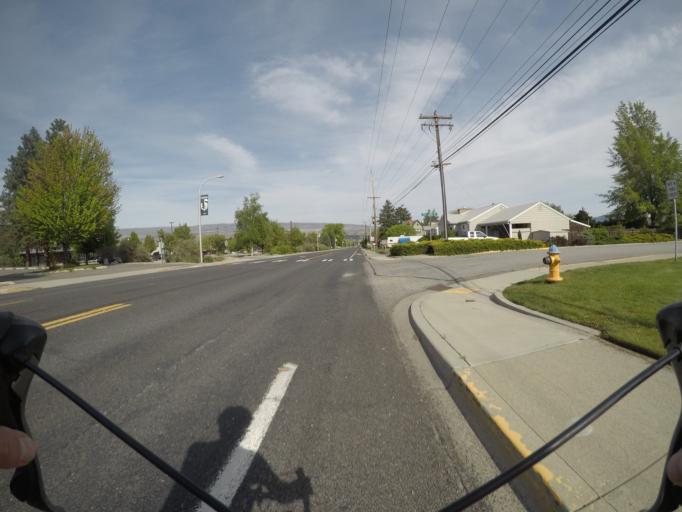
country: US
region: Washington
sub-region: Chelan County
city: West Wenatchee
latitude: 47.4298
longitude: -120.3411
